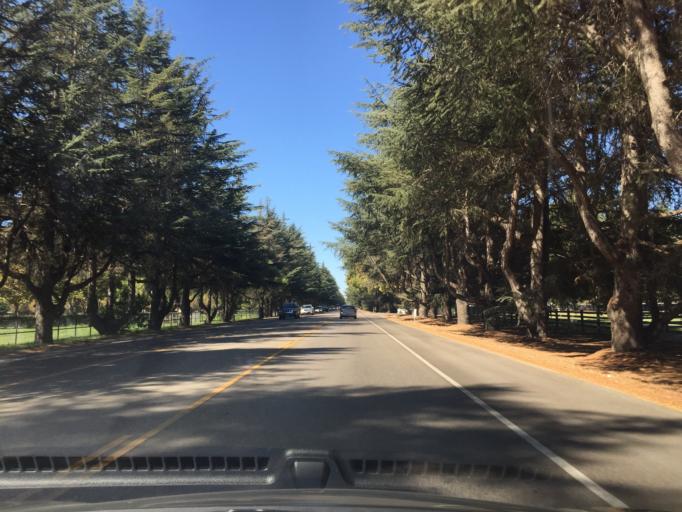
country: US
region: California
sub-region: Santa Barbara County
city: Solvang
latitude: 34.6005
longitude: -120.1628
